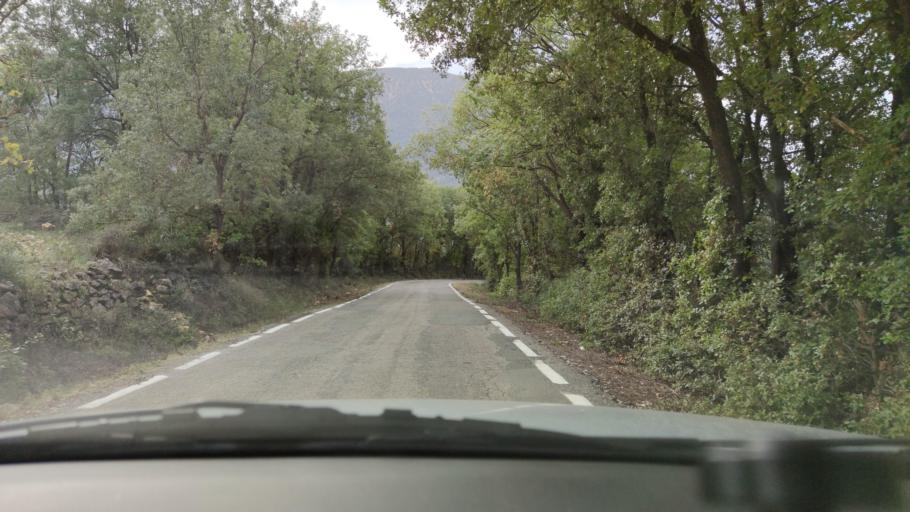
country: ES
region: Catalonia
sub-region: Provincia de Lleida
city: Llimiana
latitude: 42.0632
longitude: 0.9078
